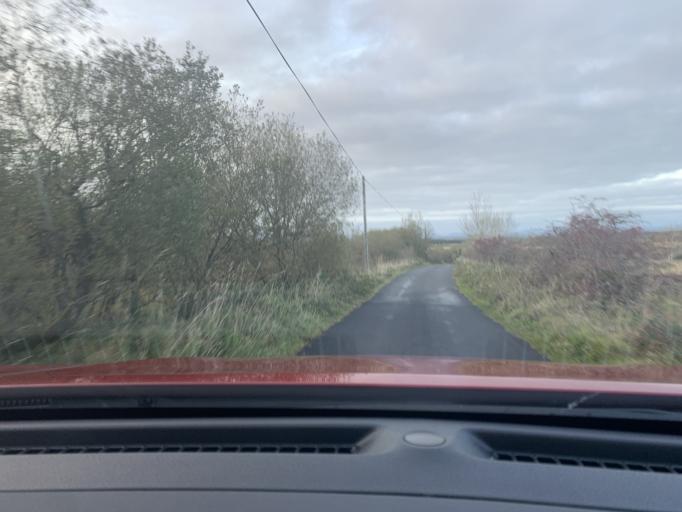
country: IE
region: Connaught
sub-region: Roscommon
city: Ballaghaderreen
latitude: 53.9544
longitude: -8.6025
